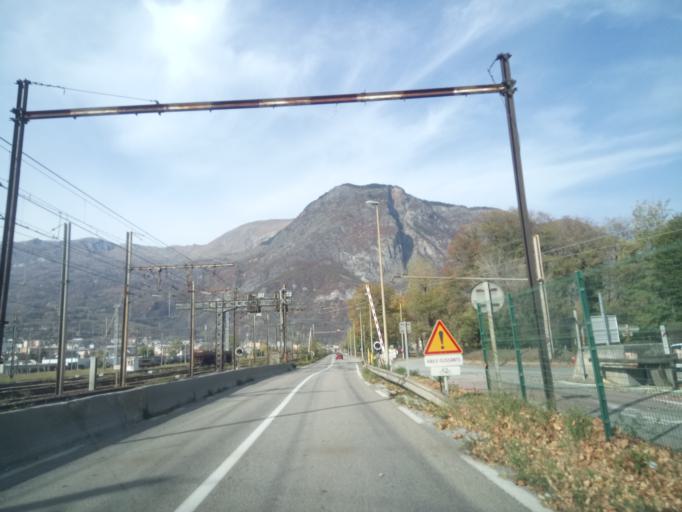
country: FR
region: Rhone-Alpes
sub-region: Departement de la Savoie
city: Villargondran
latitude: 45.2730
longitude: 6.3650
